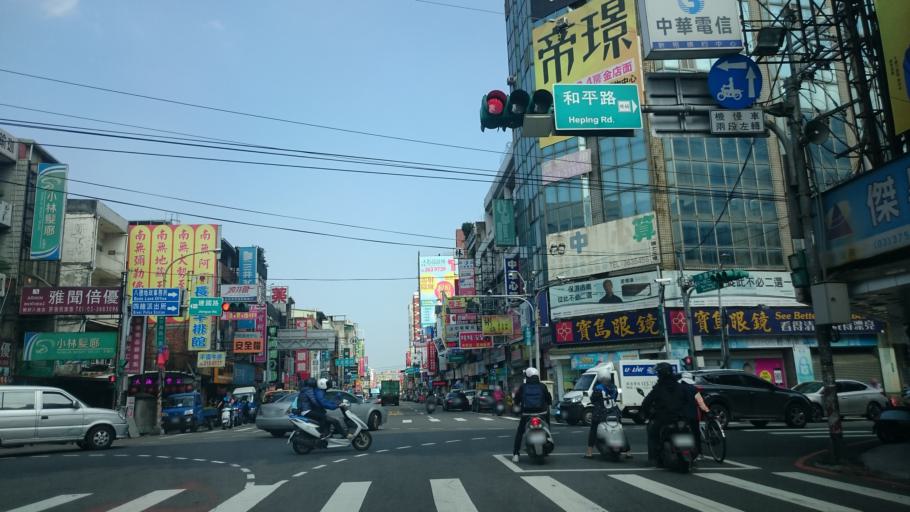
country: TW
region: Taiwan
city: Taoyuan City
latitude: 24.9574
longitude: 121.2991
